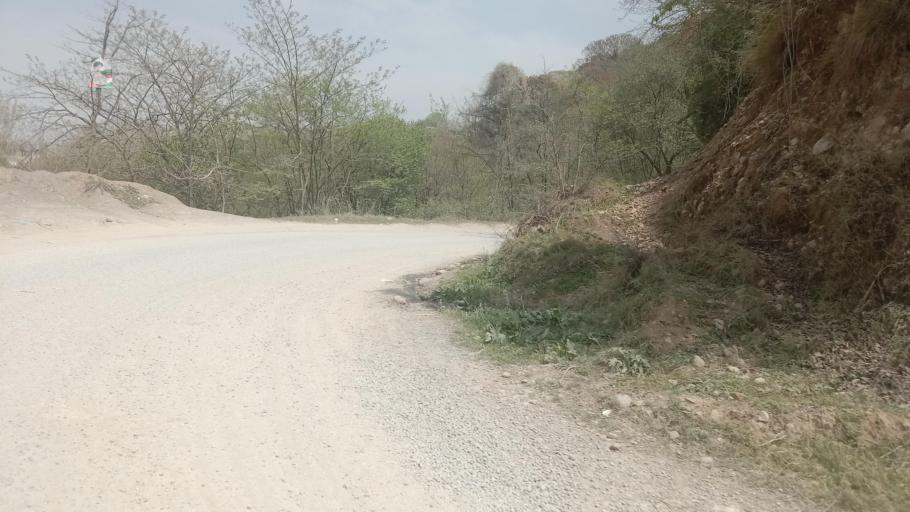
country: PK
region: Khyber Pakhtunkhwa
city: Abbottabad
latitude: 34.1582
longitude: 73.2679
